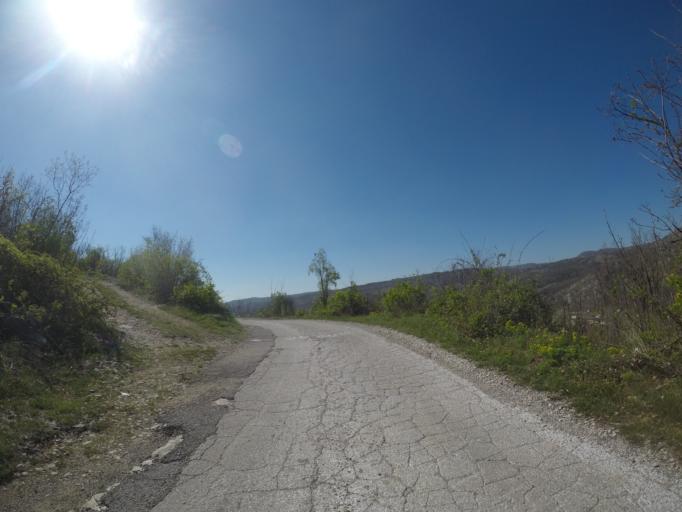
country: ME
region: Danilovgrad
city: Danilovgrad
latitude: 42.5367
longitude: 19.0146
